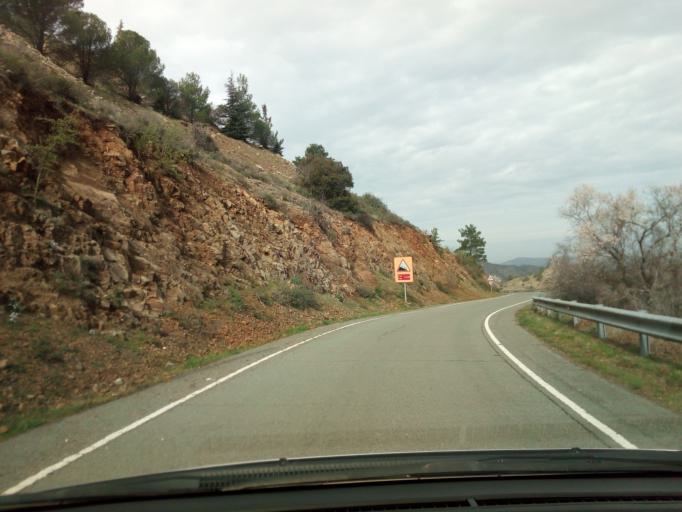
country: CY
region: Lefkosia
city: Klirou
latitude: 34.9575
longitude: 33.1696
